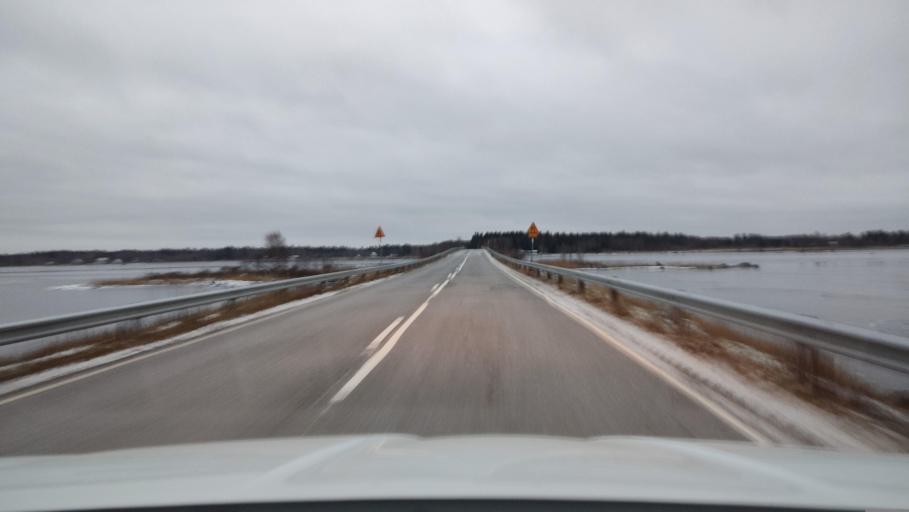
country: FI
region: Ostrobothnia
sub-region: Vaasa
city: Replot
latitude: 63.2766
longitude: 21.3439
